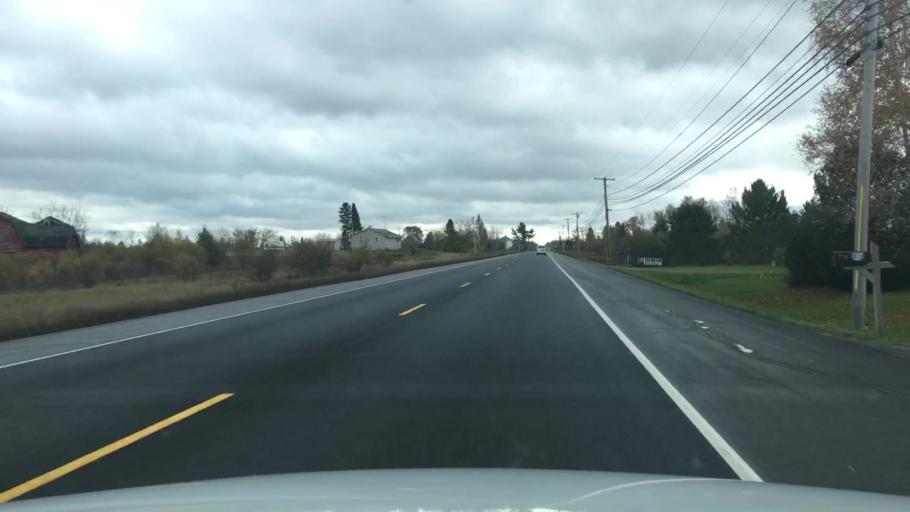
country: US
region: Maine
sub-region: Aroostook County
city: Houlton
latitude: 46.2532
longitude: -67.8408
